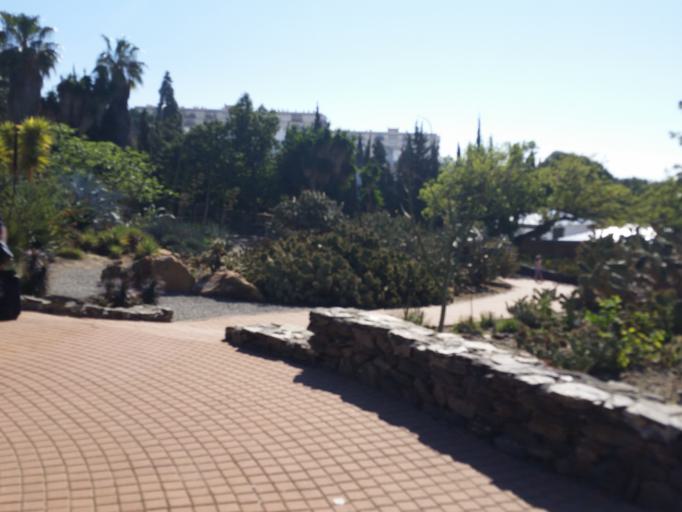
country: ES
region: Andalusia
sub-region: Provincia de Malaga
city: Torremolinos
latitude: 36.5948
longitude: -4.5291
